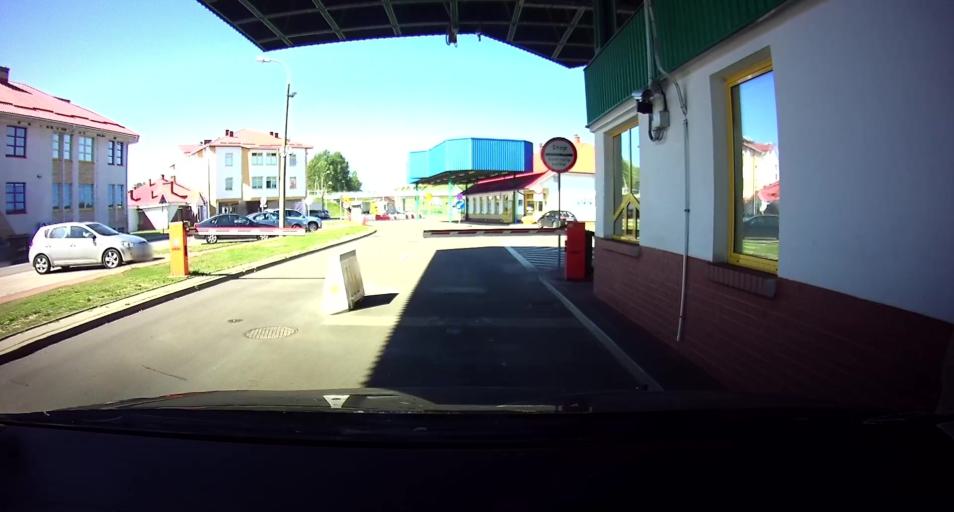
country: BY
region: Grodnenskaya
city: Vyalikaya Byerastavitsa
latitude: 53.1239
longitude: 23.8907
